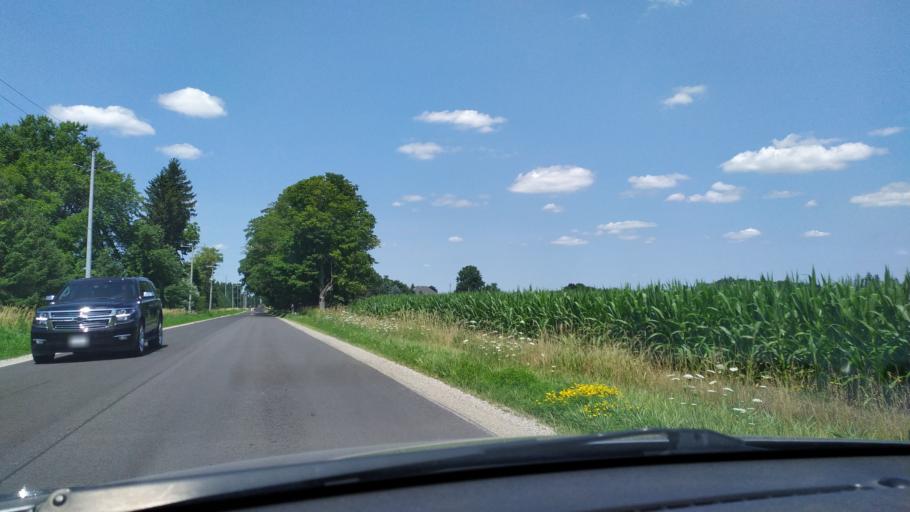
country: CA
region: Ontario
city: Stratford
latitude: 43.3564
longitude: -80.9378
